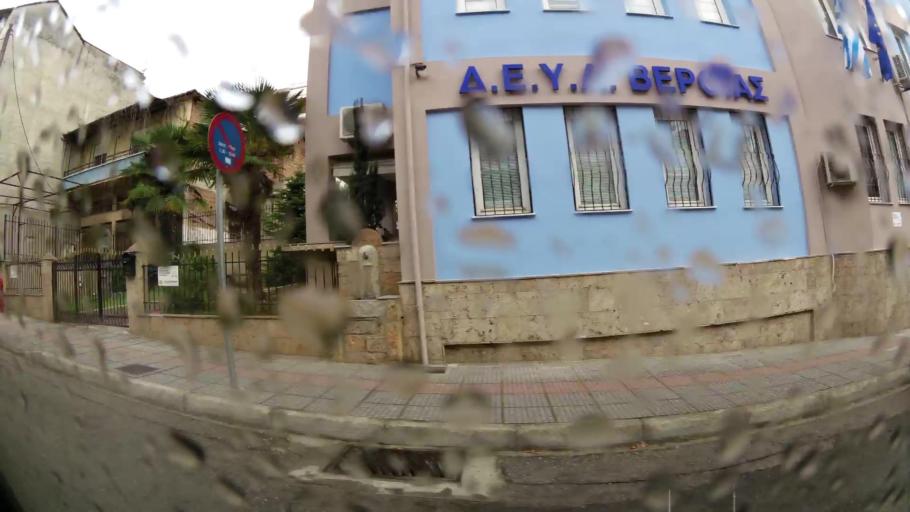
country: GR
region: Central Macedonia
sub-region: Nomos Imathias
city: Veroia
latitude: 40.5289
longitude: 22.2009
